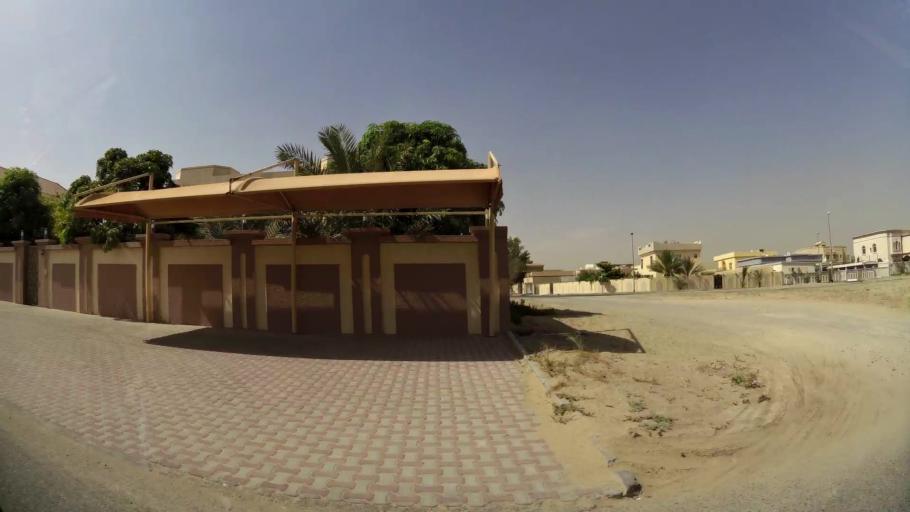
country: AE
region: Ash Shariqah
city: Sharjah
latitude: 25.1951
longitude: 55.4186
